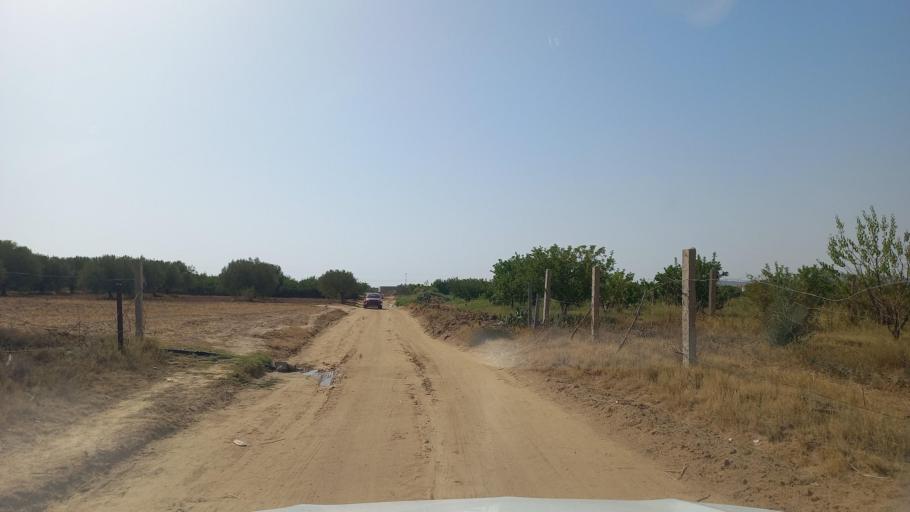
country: TN
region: Al Qasrayn
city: Kasserine
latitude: 35.2429
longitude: 9.0350
